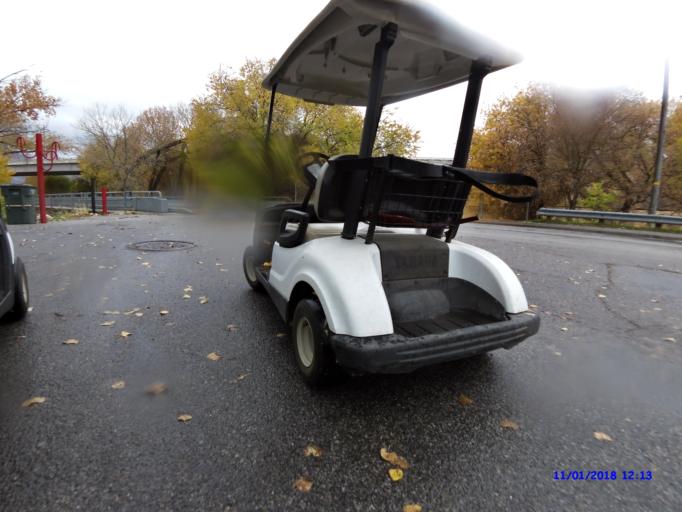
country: US
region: Utah
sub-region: Weber County
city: Ogden
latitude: 41.2236
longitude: -111.9886
